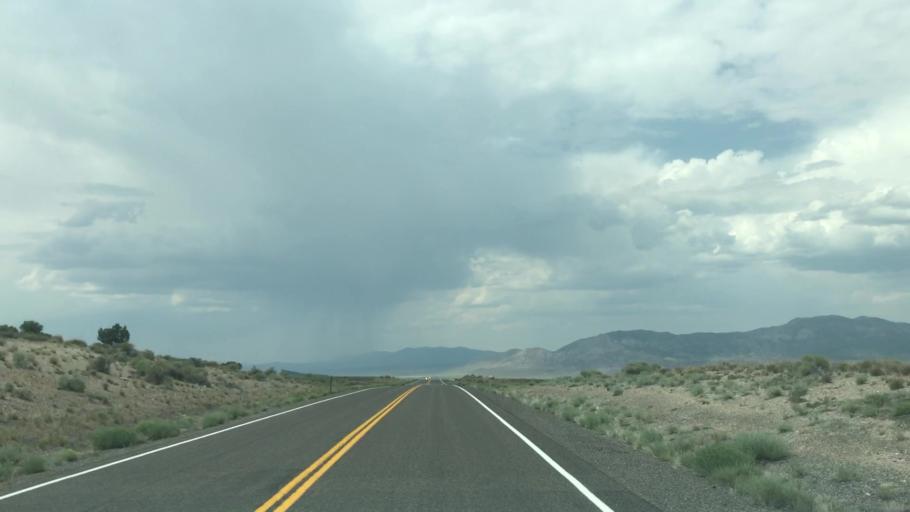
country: US
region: Nevada
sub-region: Eureka County
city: Eureka
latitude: 39.3926
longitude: -115.7295
